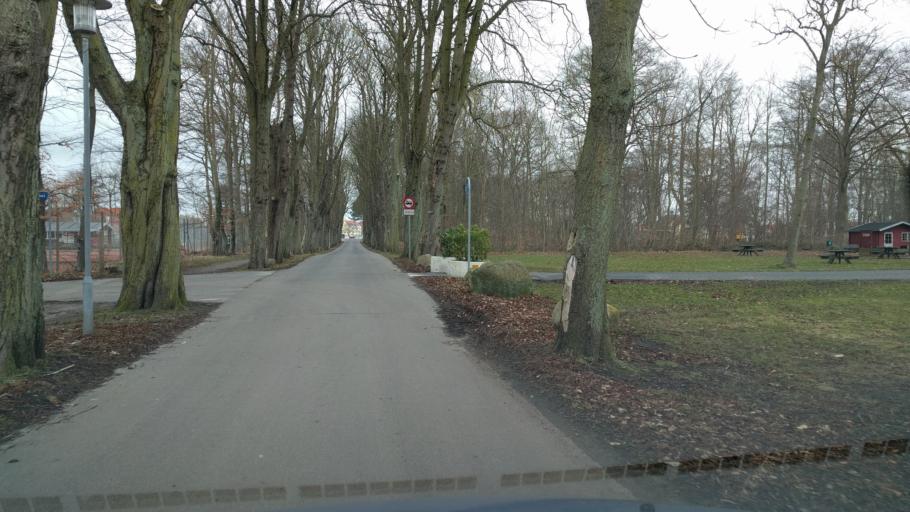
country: DK
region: South Denmark
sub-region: Kerteminde Kommune
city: Kerteminde
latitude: 55.4439
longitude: 10.6634
